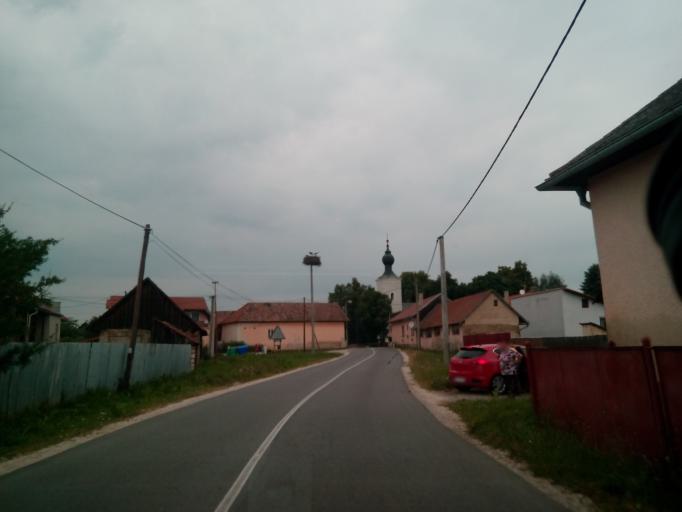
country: SK
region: Kosicky
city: Spisska Nova Ves
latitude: 48.9295
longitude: 20.6333
